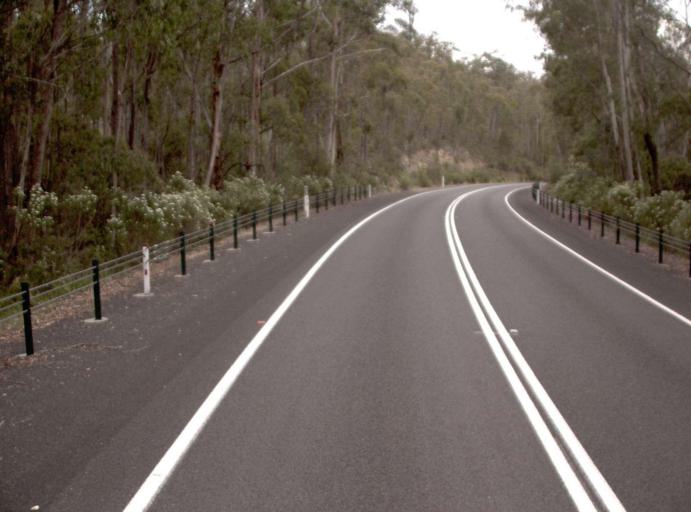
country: AU
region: New South Wales
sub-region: Bombala
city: Bombala
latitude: -37.3484
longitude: 149.2026
